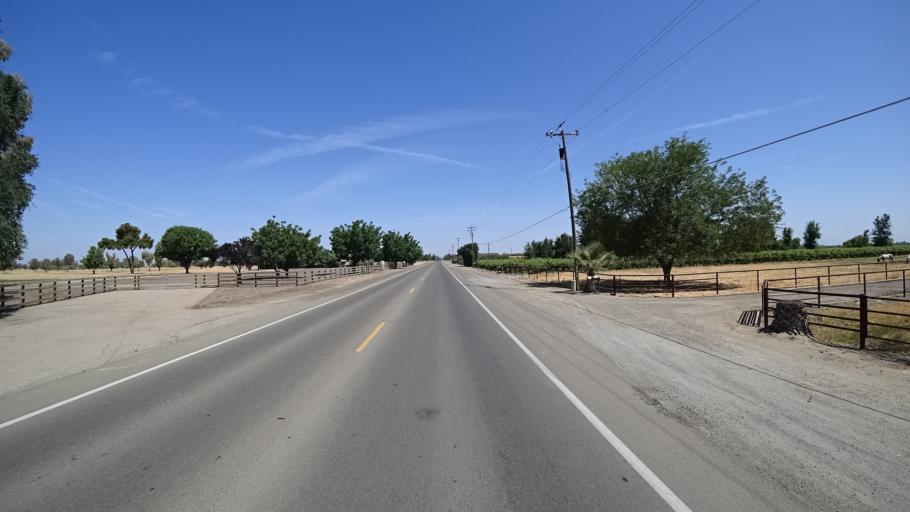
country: US
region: California
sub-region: Kings County
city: Lemoore
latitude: 36.2564
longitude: -119.7809
